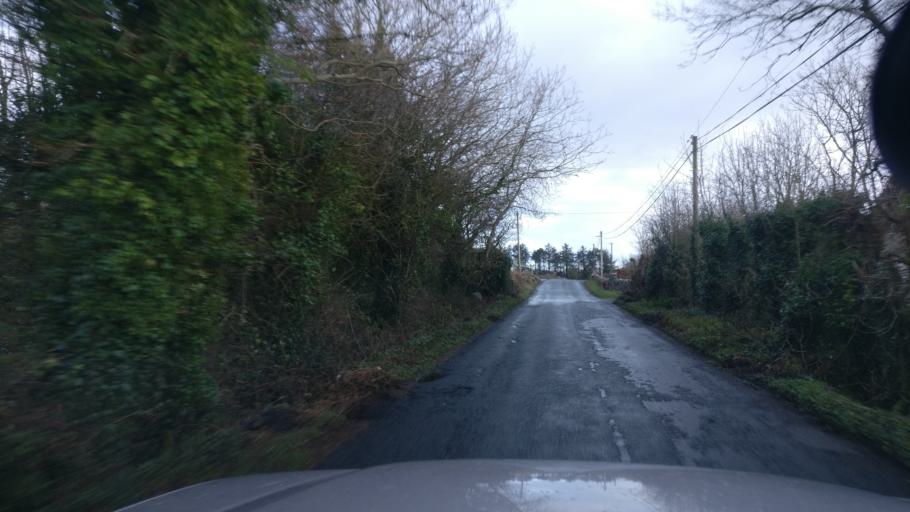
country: IE
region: Connaught
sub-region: County Galway
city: Athenry
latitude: 53.2979
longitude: -8.7070
